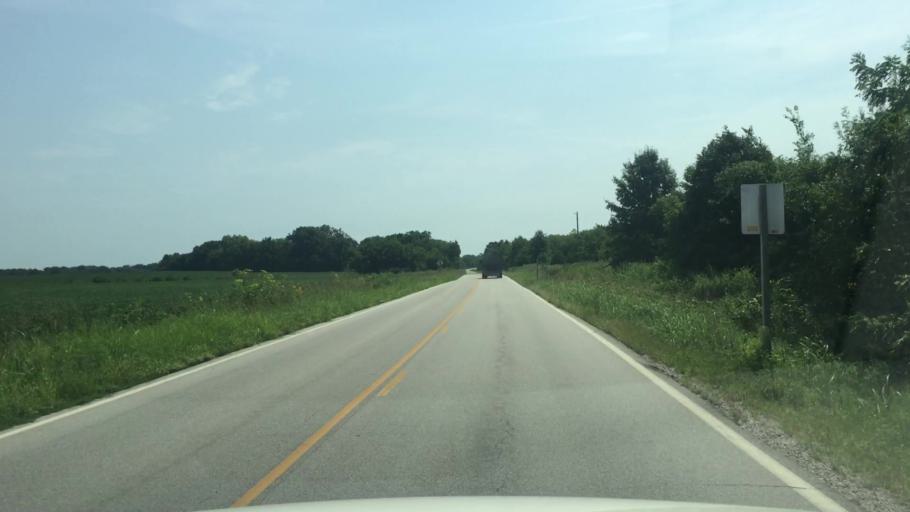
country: US
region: Kansas
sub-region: Montgomery County
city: Cherryvale
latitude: 37.1938
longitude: -95.5560
